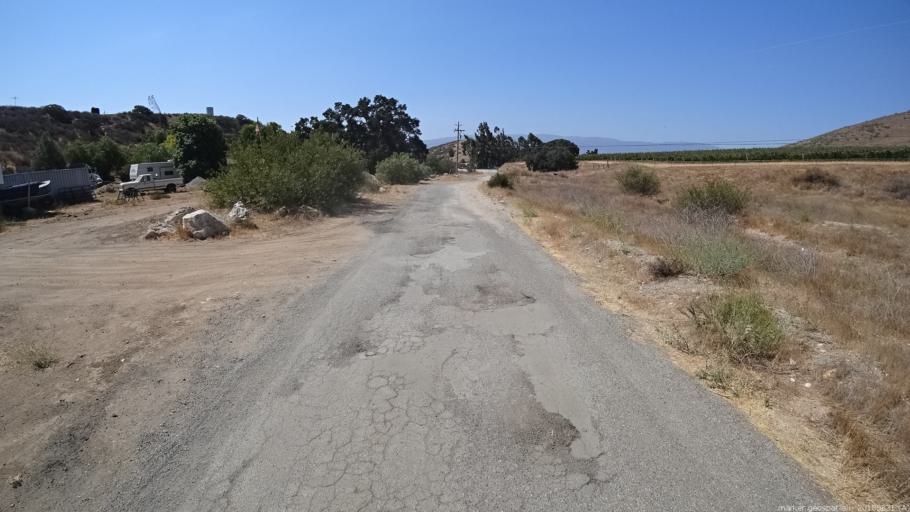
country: US
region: California
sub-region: Monterey County
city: Soledad
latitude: 36.4482
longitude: -121.2982
